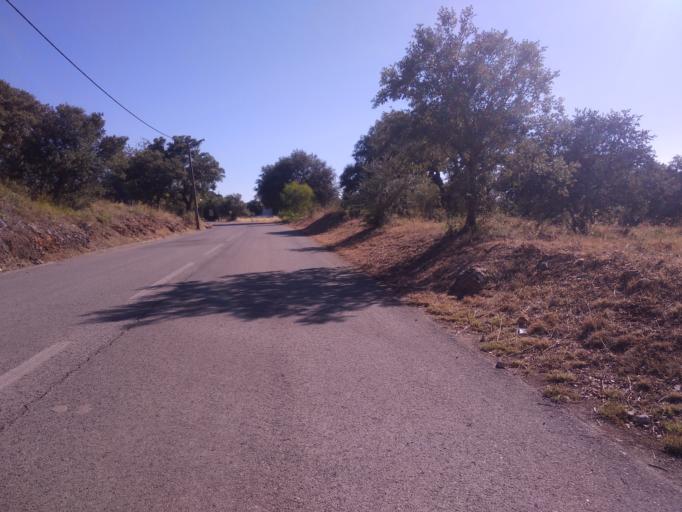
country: PT
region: Faro
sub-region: Sao Bras de Alportel
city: Sao Bras de Alportel
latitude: 37.1708
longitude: -7.8835
